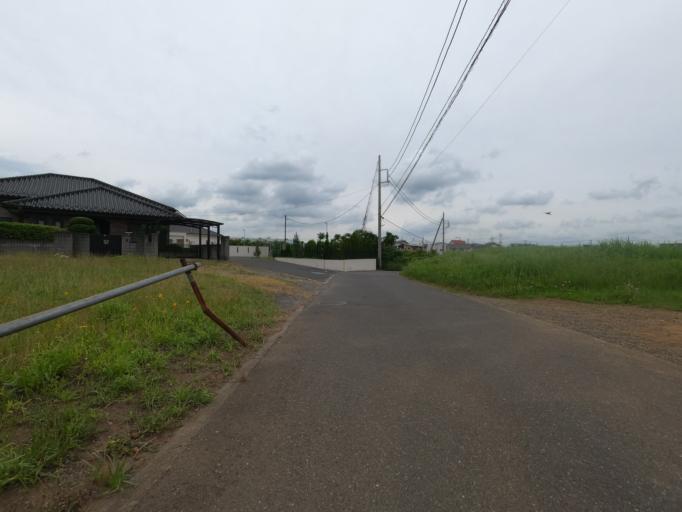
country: JP
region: Ibaraki
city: Moriya
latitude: 35.9541
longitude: 139.9850
